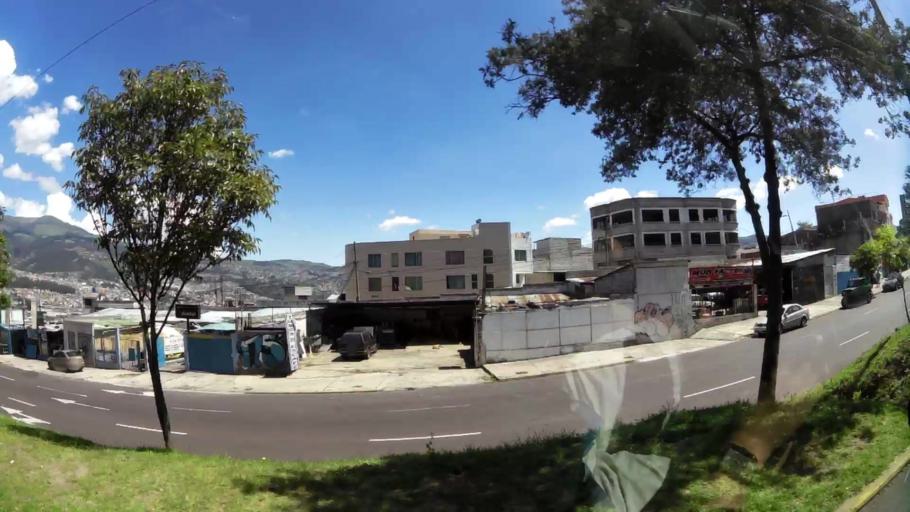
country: EC
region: Pichincha
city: Quito
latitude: -0.1051
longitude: -78.4835
